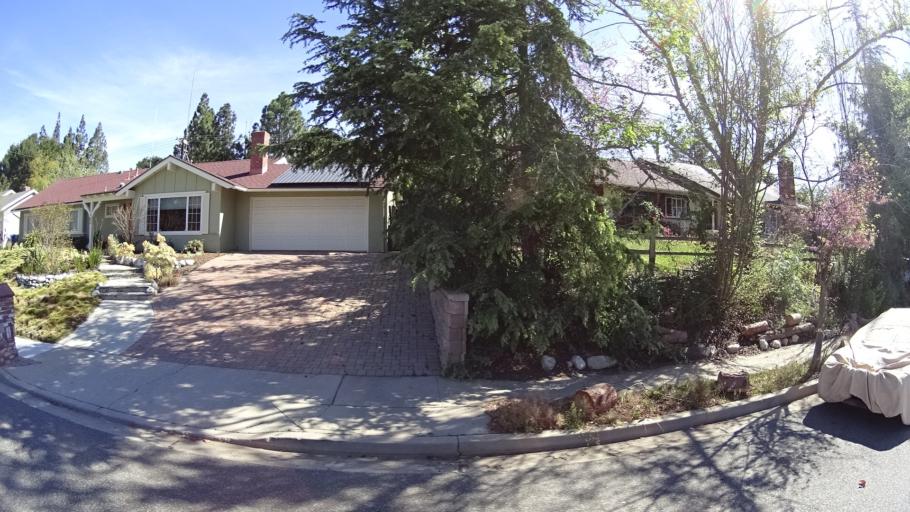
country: US
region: California
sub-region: Ventura County
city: Thousand Oaks
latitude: 34.2251
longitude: -118.8600
